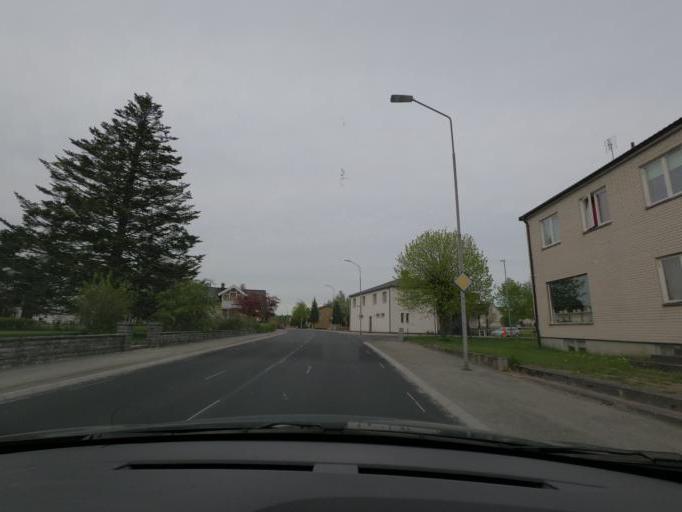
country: SE
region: Joenkoeping
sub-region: Varnamo Kommun
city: Bredaryd
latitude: 57.2203
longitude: 13.7826
